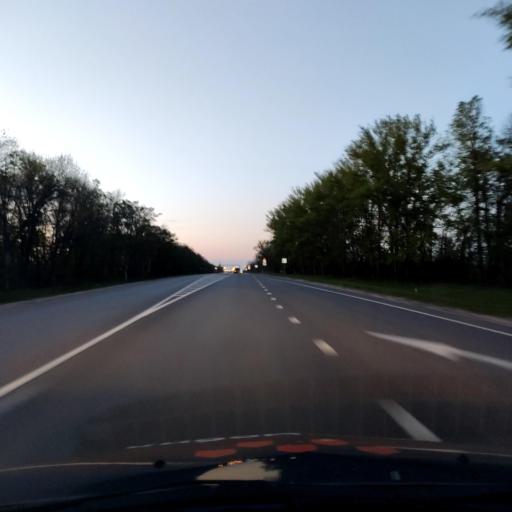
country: RU
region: Orjol
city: Zmiyevka
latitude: 52.7082
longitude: 36.3588
